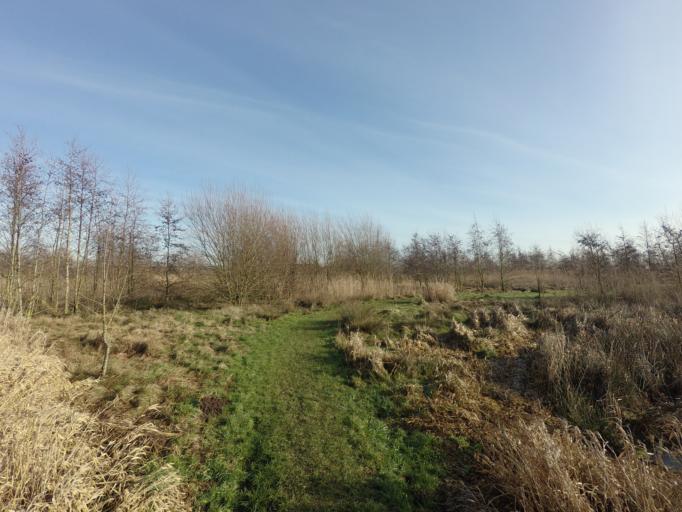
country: NL
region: Utrecht
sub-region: Gemeente Oudewater
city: Oudewater
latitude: 52.0328
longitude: 4.8558
